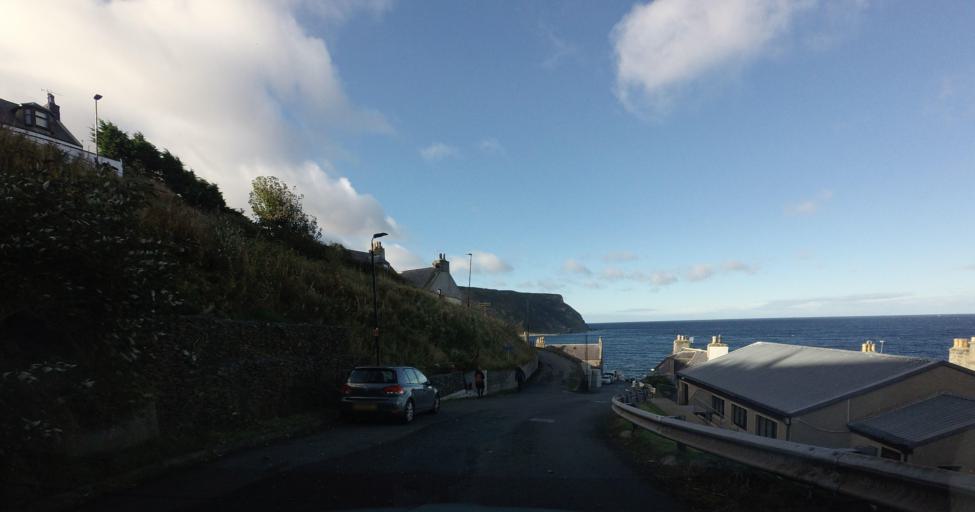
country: GB
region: Scotland
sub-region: Aberdeenshire
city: Macduff
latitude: 57.6719
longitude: -2.3366
